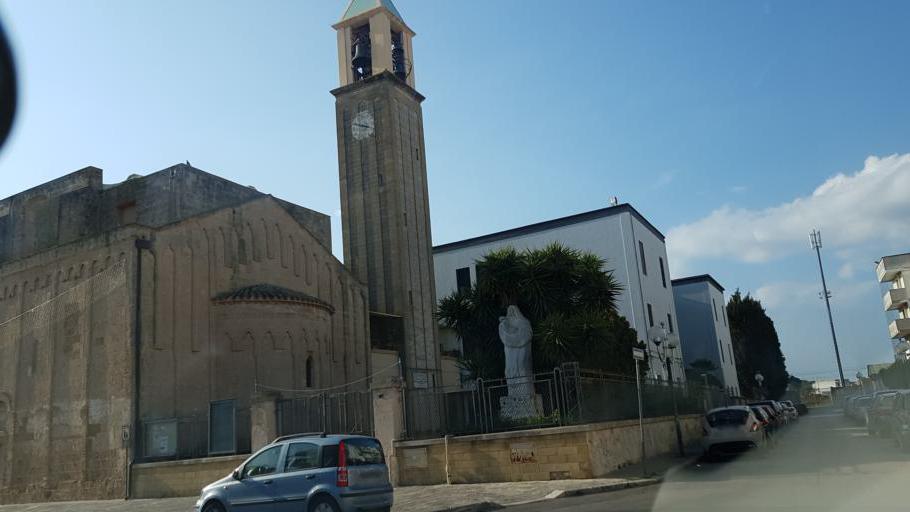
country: IT
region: Apulia
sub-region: Provincia di Brindisi
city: Mesagne
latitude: 40.5619
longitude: 17.8024
